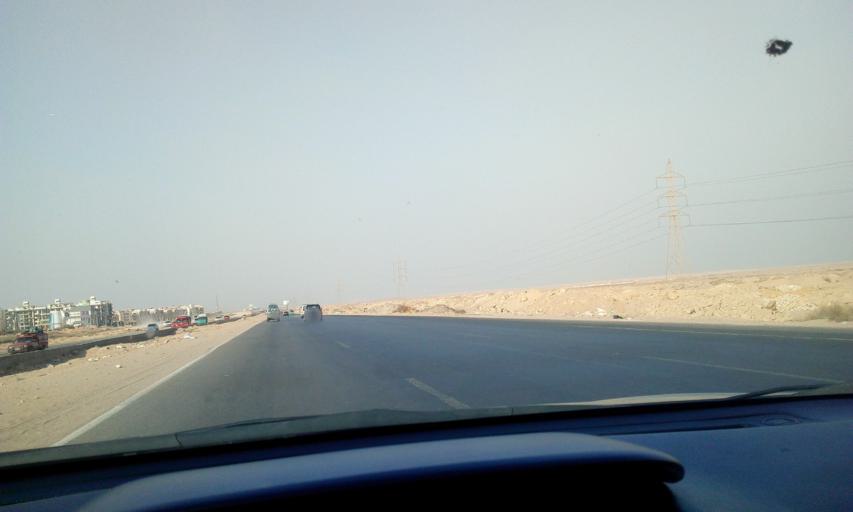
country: EG
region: Al Jizah
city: Madinat Sittah Uktubar
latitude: 29.8854
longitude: 31.0797
